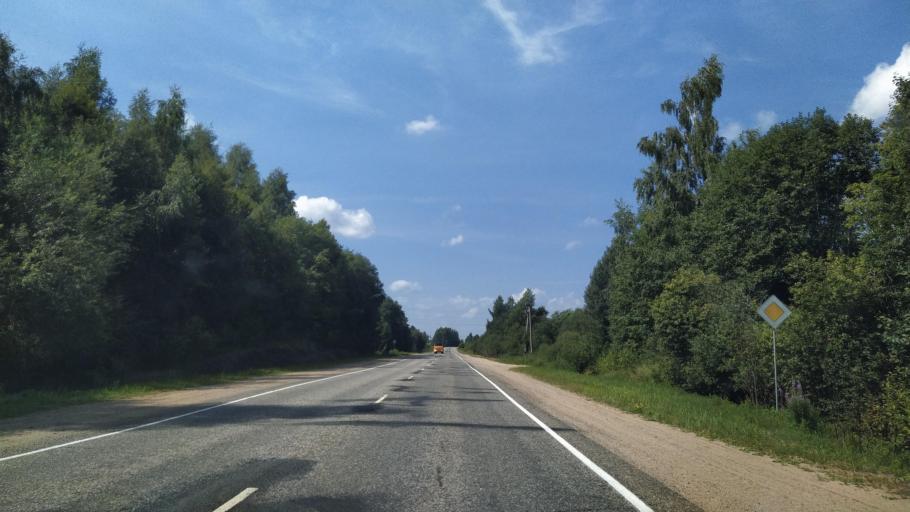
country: RU
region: Pskov
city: Pushkinskiye Gory
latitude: 57.0117
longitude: 28.9188
